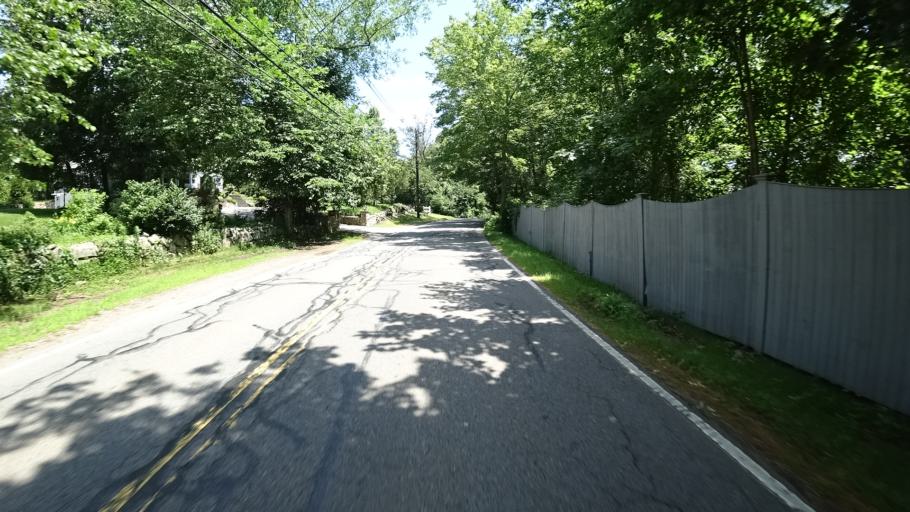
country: US
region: Massachusetts
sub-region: Norfolk County
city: Needham
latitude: 42.2516
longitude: -71.2145
